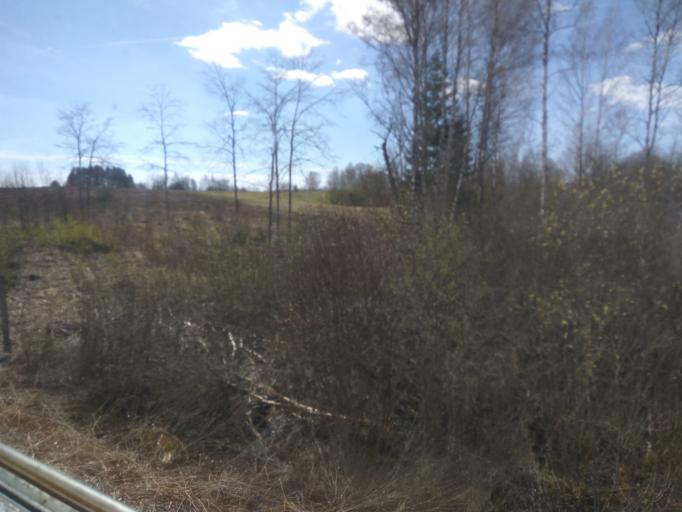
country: LV
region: Aluksnes Rajons
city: Aluksne
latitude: 57.3637
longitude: 27.0329
